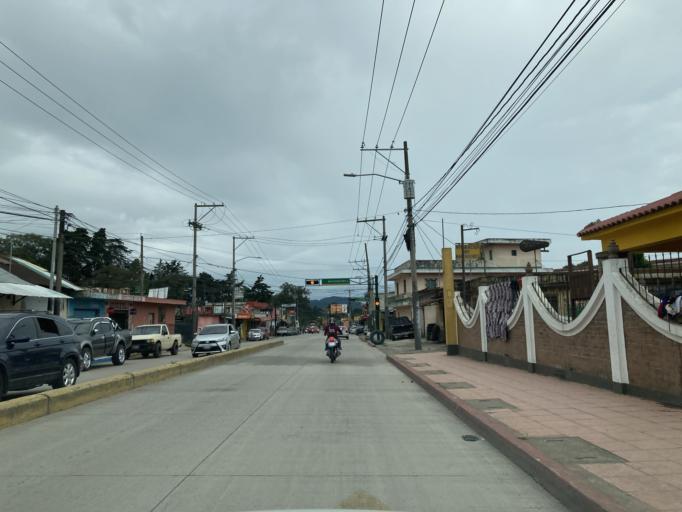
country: GT
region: Guatemala
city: San Jose Pinula
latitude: 14.5423
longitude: -90.4083
